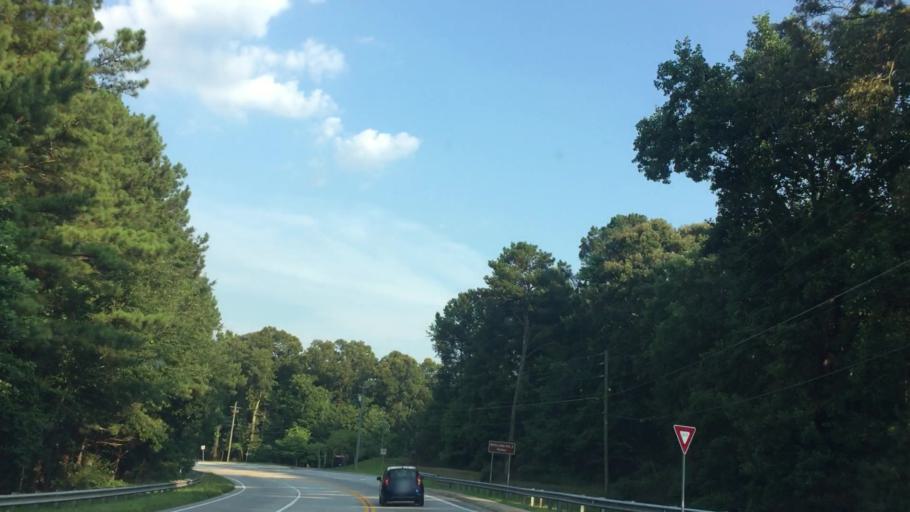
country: US
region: Georgia
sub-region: DeKalb County
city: Pine Mountain
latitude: 33.6654
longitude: -84.1973
